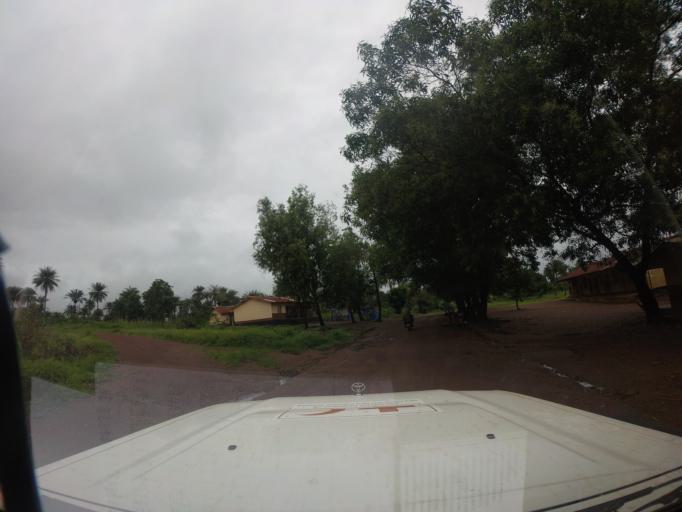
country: SL
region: Northern Province
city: Kambia
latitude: 9.1882
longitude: -12.8776
